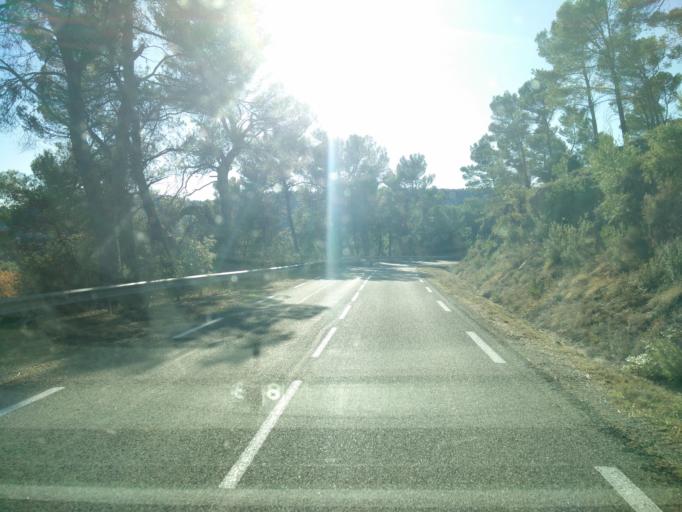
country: FR
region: Provence-Alpes-Cote d'Azur
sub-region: Departement du Var
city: Salernes
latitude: 43.5761
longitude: 6.2212
